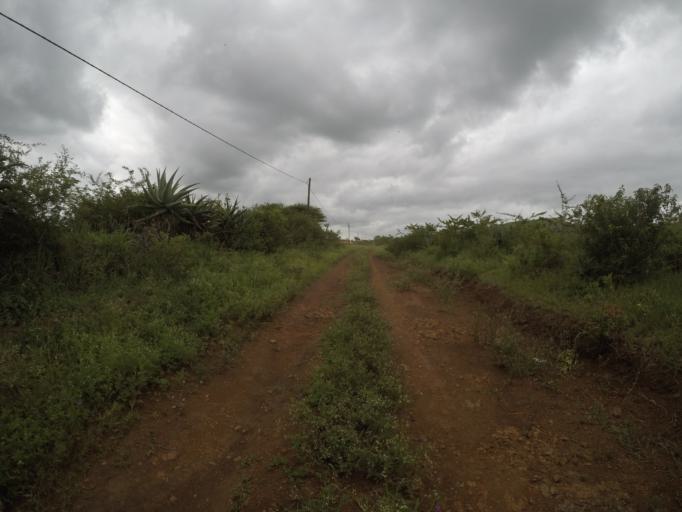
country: ZA
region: KwaZulu-Natal
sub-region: uThungulu District Municipality
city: Empangeni
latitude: -28.5887
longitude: 31.8614
